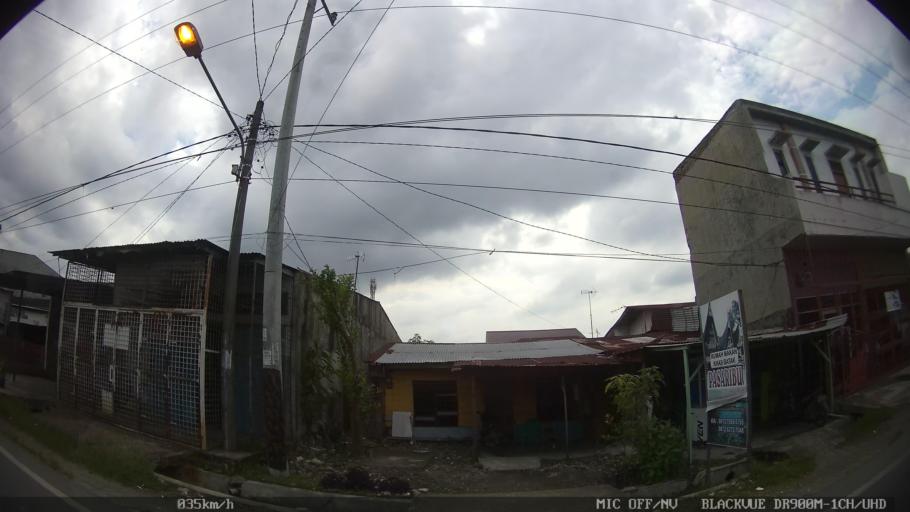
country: ID
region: North Sumatra
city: Sunggal
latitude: 3.6167
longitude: 98.6240
